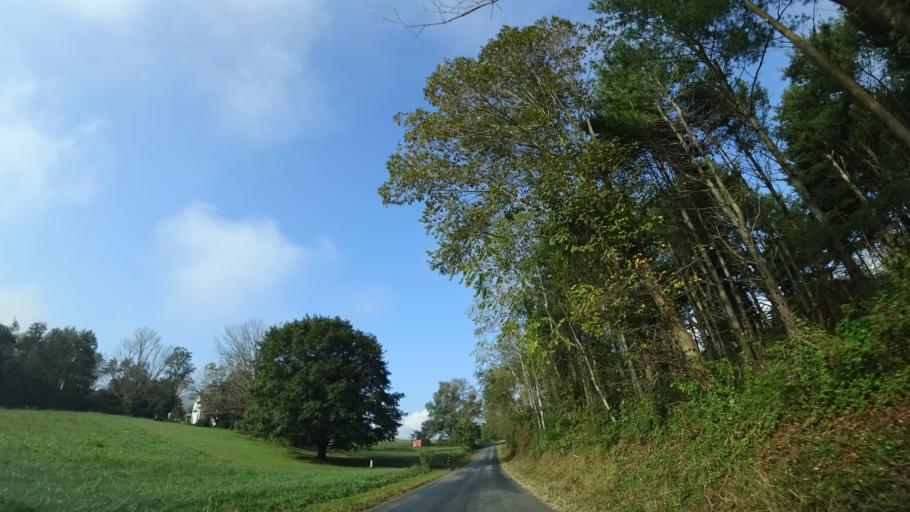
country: US
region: Virginia
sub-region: Madison County
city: Brightwood
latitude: 38.5265
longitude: -78.2701
